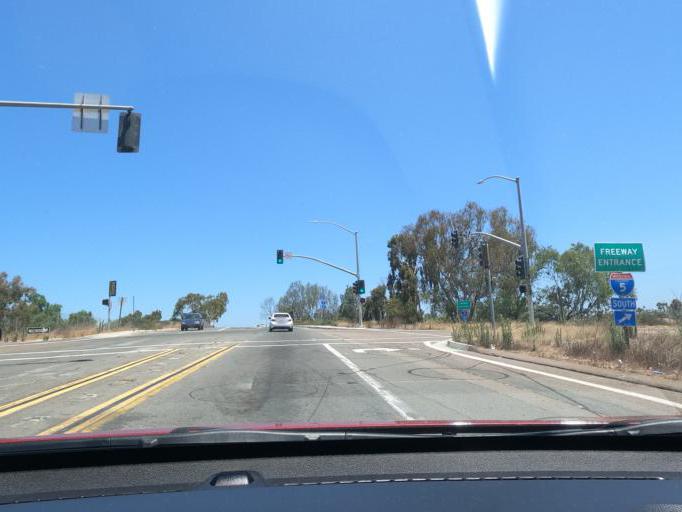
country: US
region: California
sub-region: San Diego County
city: Imperial Beach
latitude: 32.5575
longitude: -117.0624
